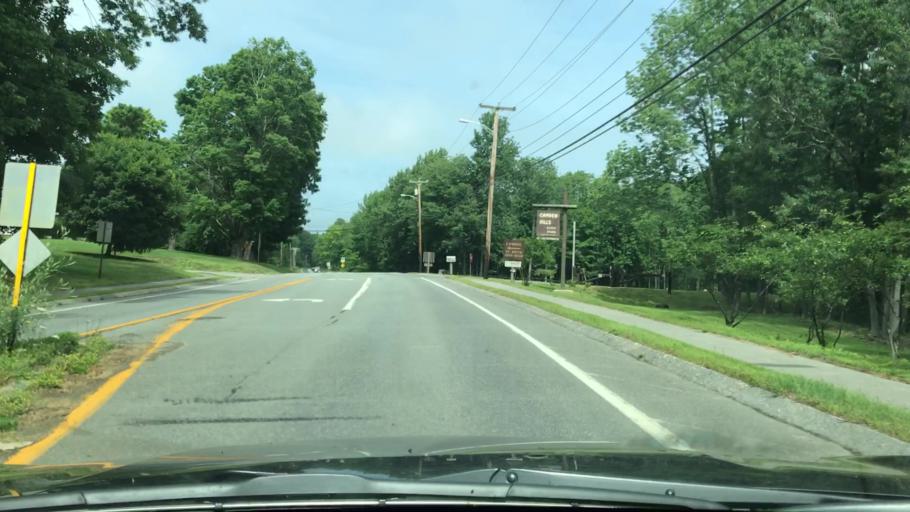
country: US
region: Maine
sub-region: Knox County
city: Camden
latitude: 44.2296
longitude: -69.0477
